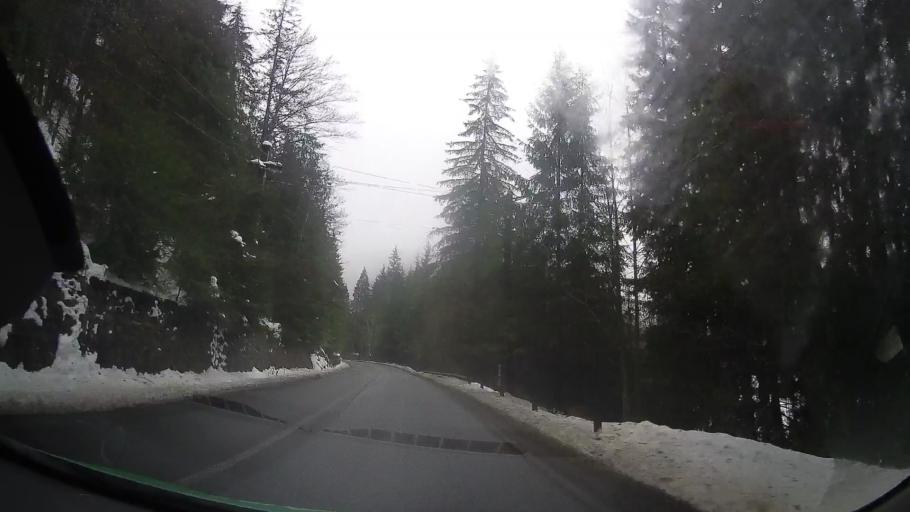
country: RO
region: Neamt
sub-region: Comuna Bicaz Chei
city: Bicaz Chei
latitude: 46.7835
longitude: 25.7866
